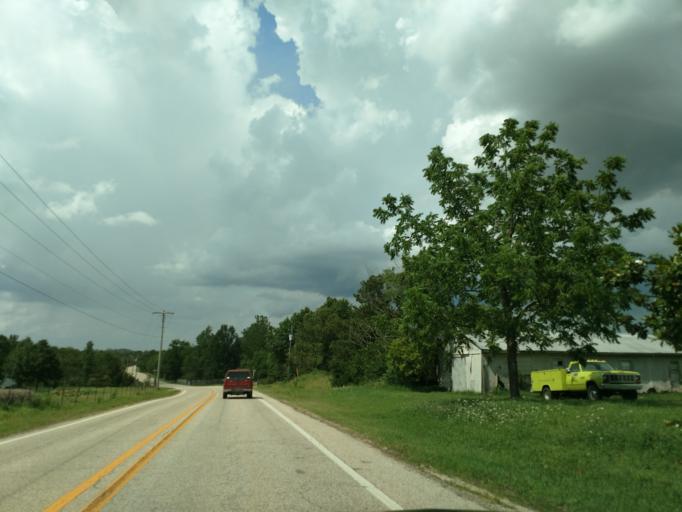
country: US
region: Arkansas
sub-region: Boone County
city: Harrison
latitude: 36.2769
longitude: -93.2345
